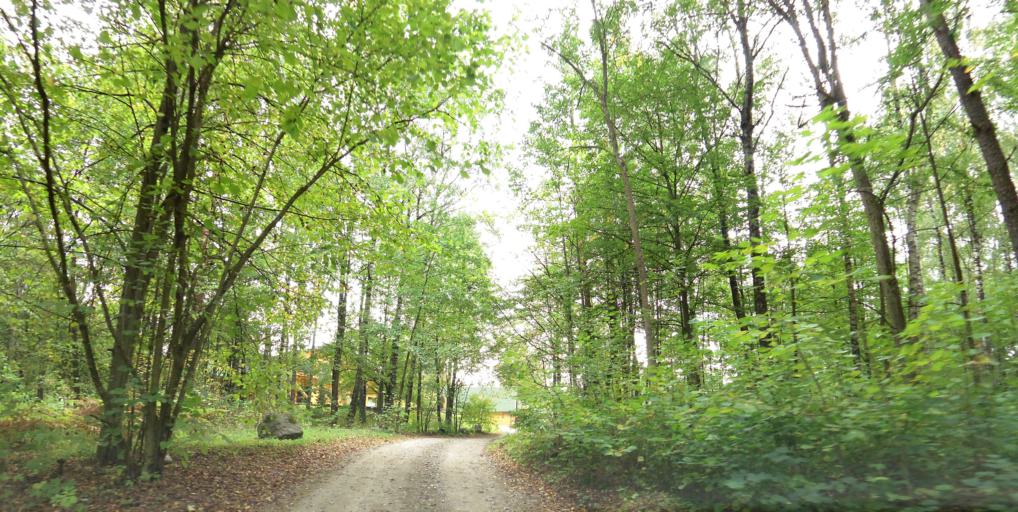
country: LT
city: Grigiskes
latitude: 54.7505
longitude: 25.0353
